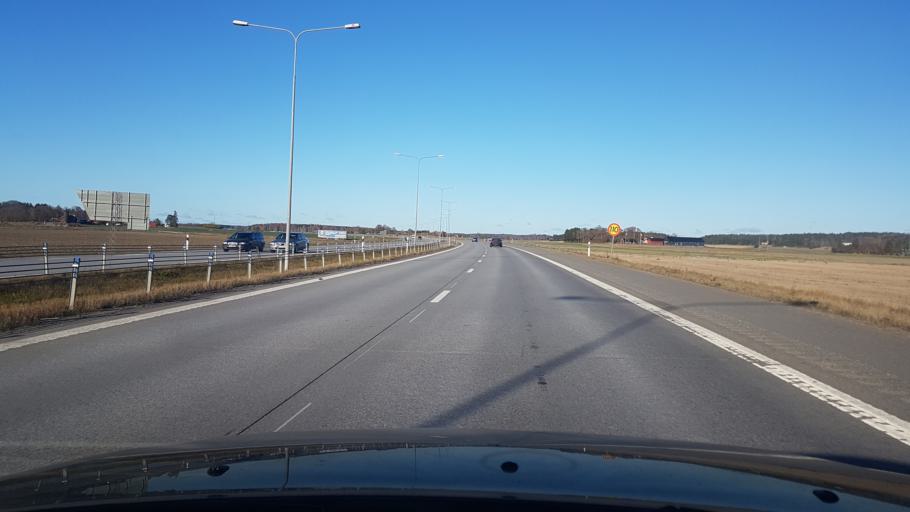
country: SE
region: Uppsala
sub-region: Uppsala Kommun
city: Saevja
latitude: 59.8518
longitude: 17.7336
